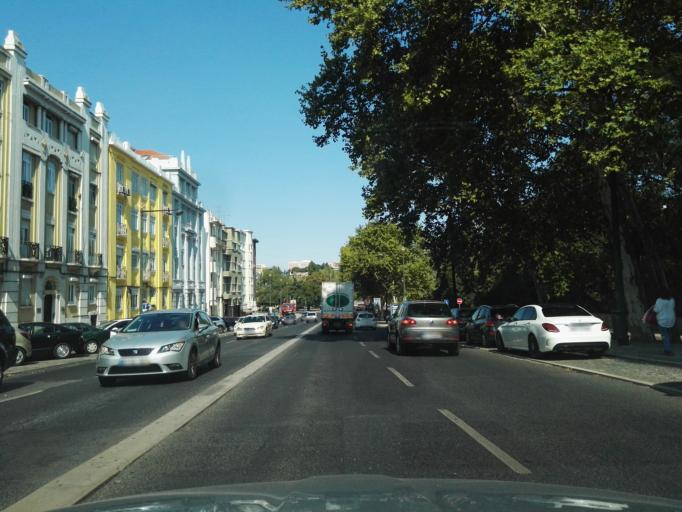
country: PT
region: Lisbon
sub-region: Lisbon
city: Lisbon
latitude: 38.7356
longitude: -9.1551
